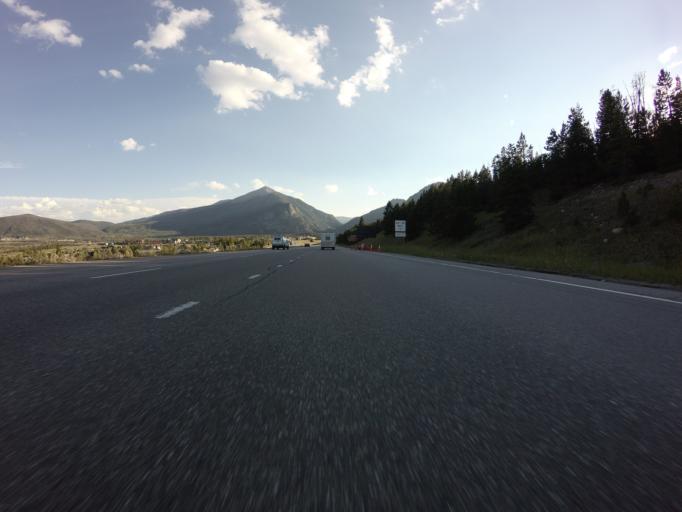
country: US
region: Colorado
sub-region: Summit County
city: Frisco
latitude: 39.5981
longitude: -106.0919
